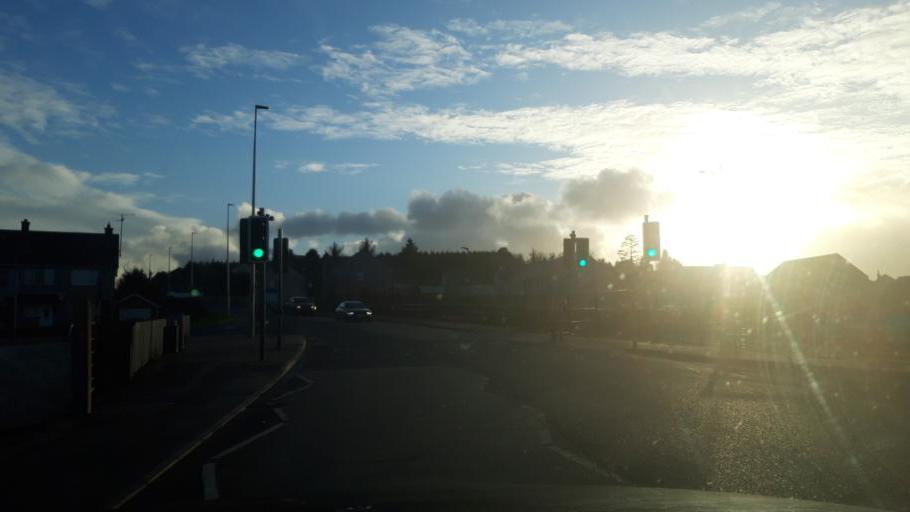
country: GB
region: Northern Ireland
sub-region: Dungannon District
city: Dungannon
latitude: 54.5137
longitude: -6.7694
